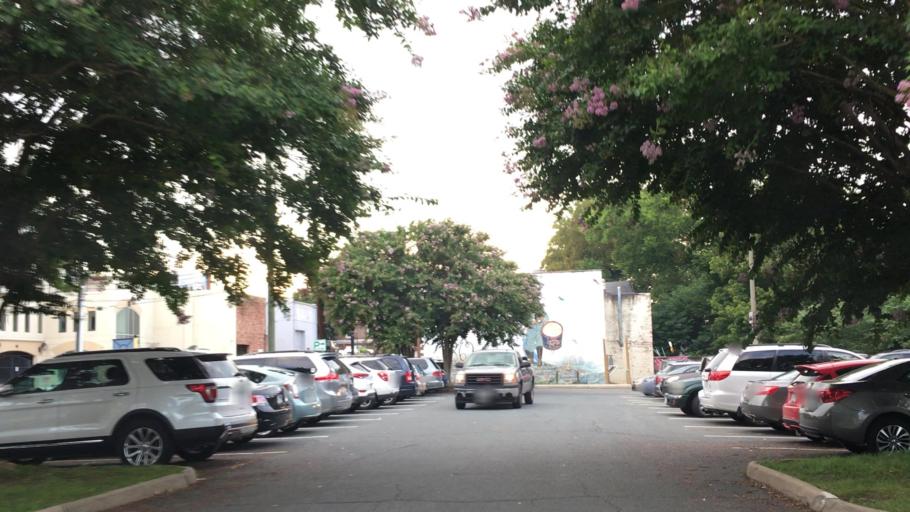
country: US
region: Virginia
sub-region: City of Fredericksburg
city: Fredericksburg
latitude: 38.3031
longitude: -77.4578
